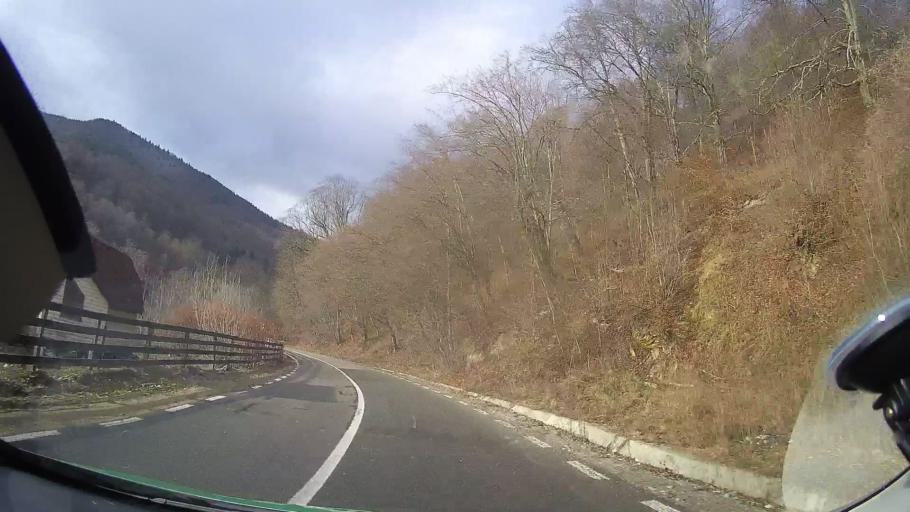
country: RO
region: Cluj
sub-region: Comuna Valea Ierii
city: Valea Ierii
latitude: 46.6415
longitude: 23.3565
